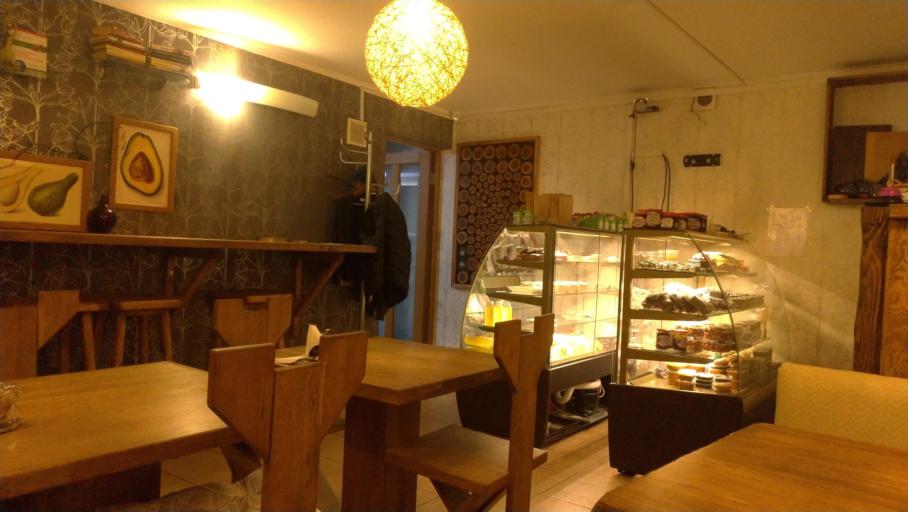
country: RU
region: Krasnodarskiy
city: Adler
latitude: 43.4409
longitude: 39.9369
